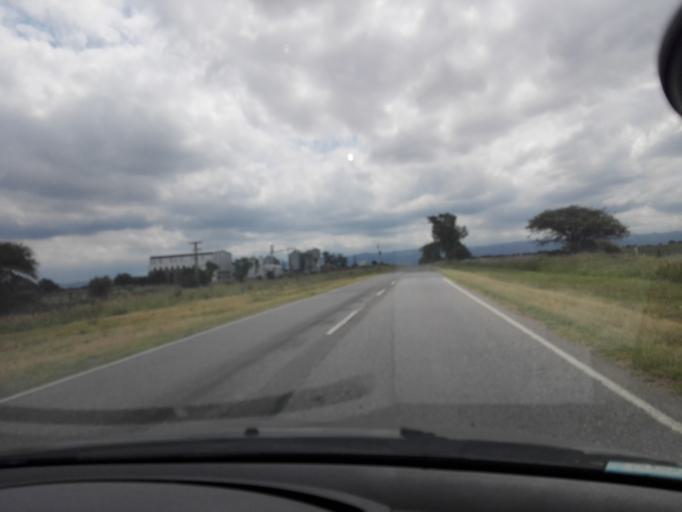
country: AR
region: Cordoba
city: Alta Gracia
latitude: -31.6581
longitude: -64.3729
